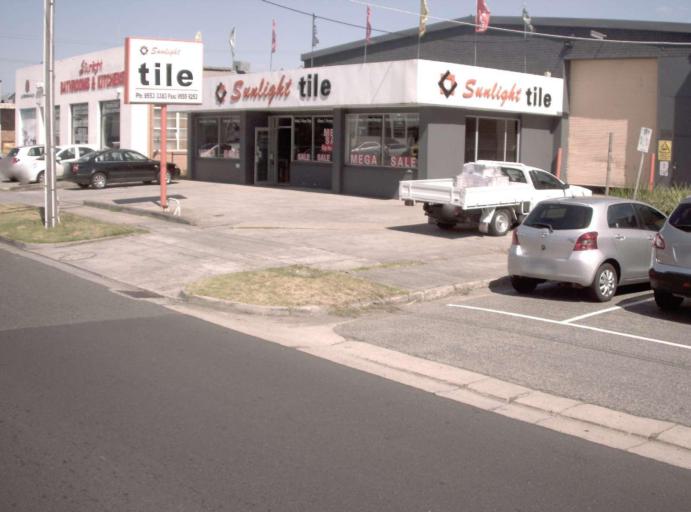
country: AU
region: Victoria
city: Highett
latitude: -37.9464
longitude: 145.0529
